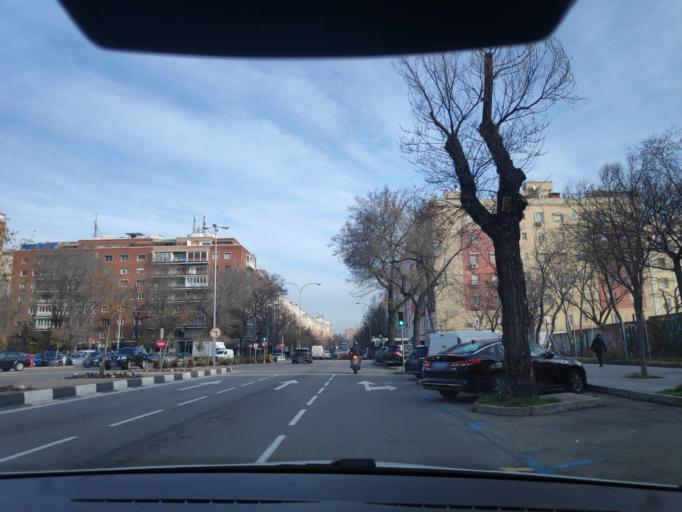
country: ES
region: Madrid
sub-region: Provincia de Madrid
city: Chamartin
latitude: 40.4547
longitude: -3.6771
